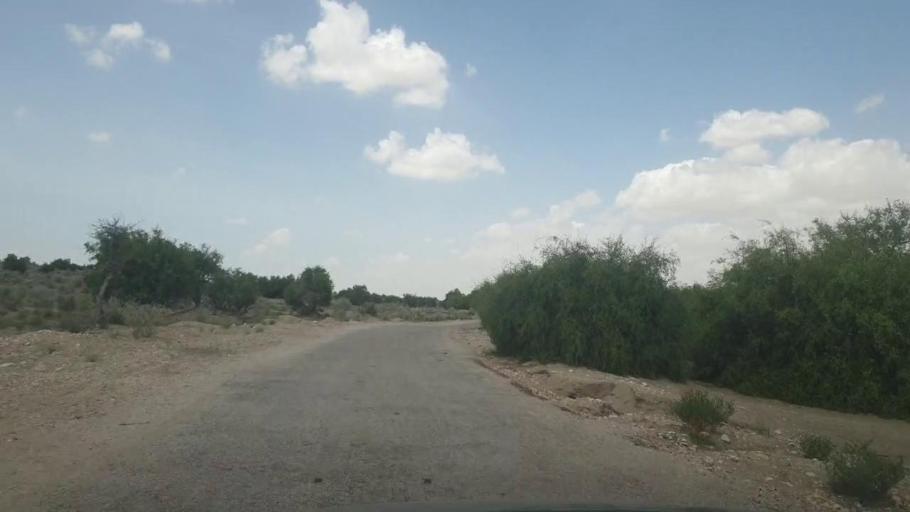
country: PK
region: Sindh
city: Kot Diji
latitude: 27.2195
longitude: 69.1021
